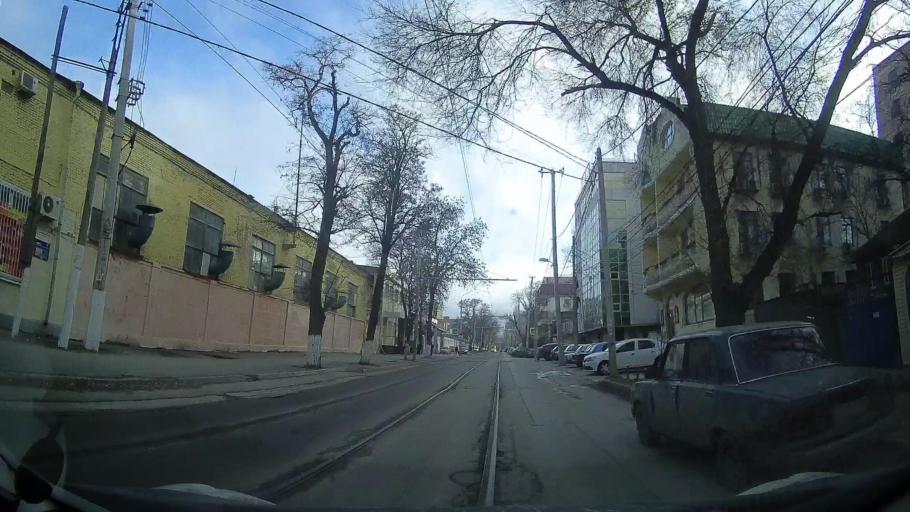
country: RU
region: Rostov
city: Rostov-na-Donu
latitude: 47.2347
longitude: 39.7330
